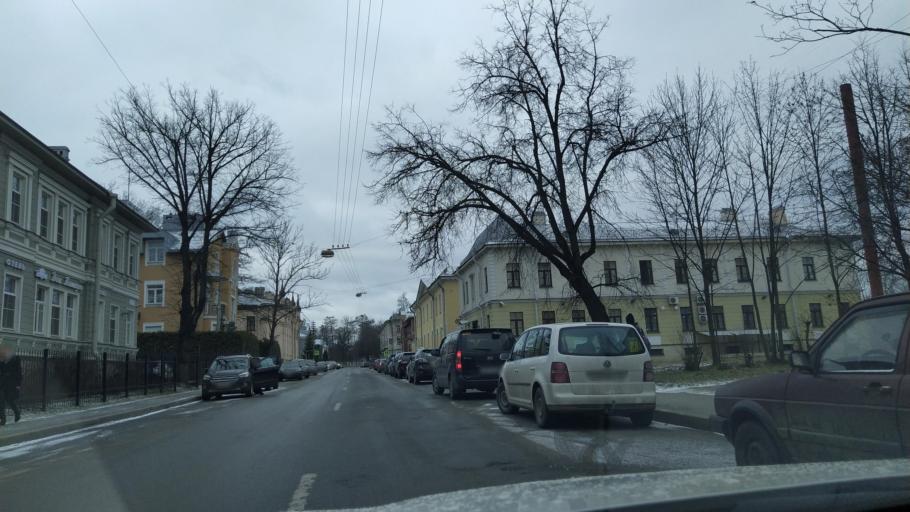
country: RU
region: St.-Petersburg
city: Pushkin
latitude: 59.7194
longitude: 30.4012
